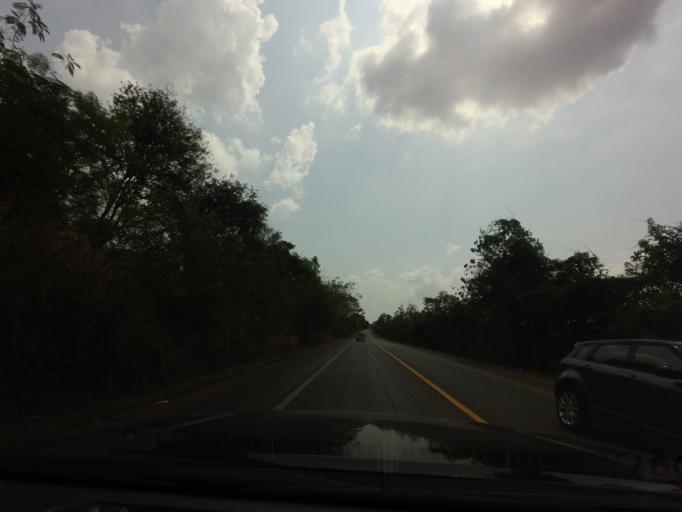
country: TH
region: Kanchanaburi
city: Sai Yok
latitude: 14.1539
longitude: 99.1410
